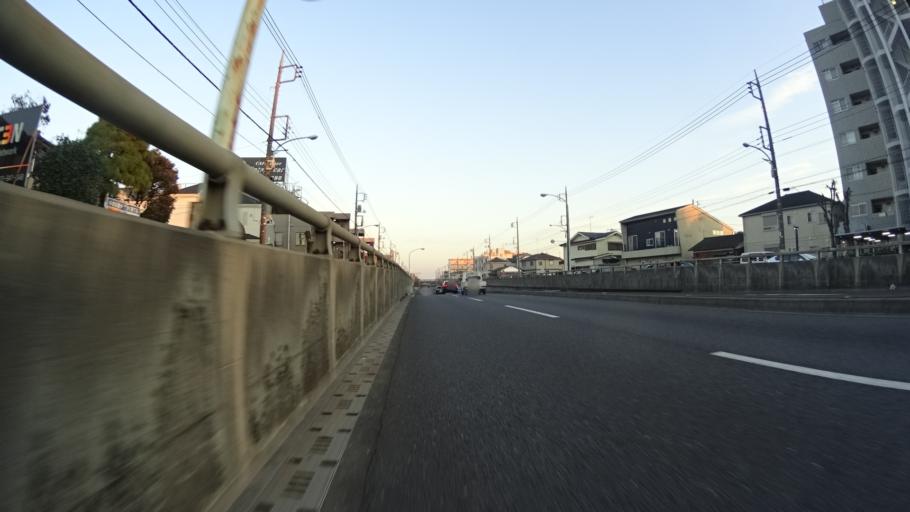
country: JP
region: Tokyo
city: Hino
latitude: 35.7016
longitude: 139.3598
